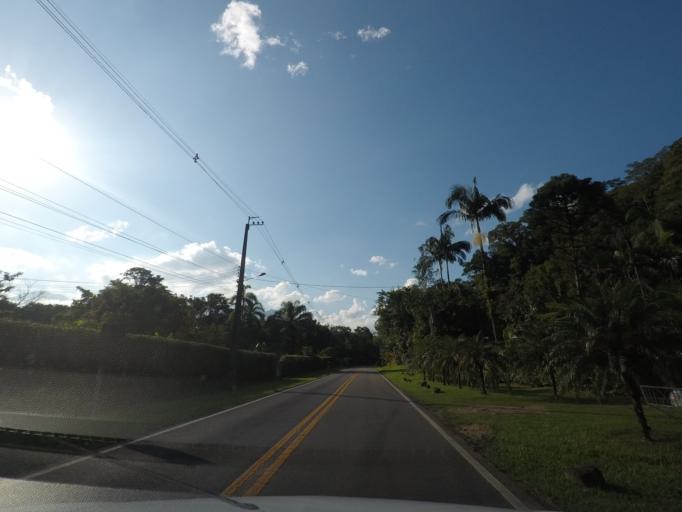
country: BR
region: Parana
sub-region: Antonina
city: Antonina
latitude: -25.4251
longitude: -48.8765
